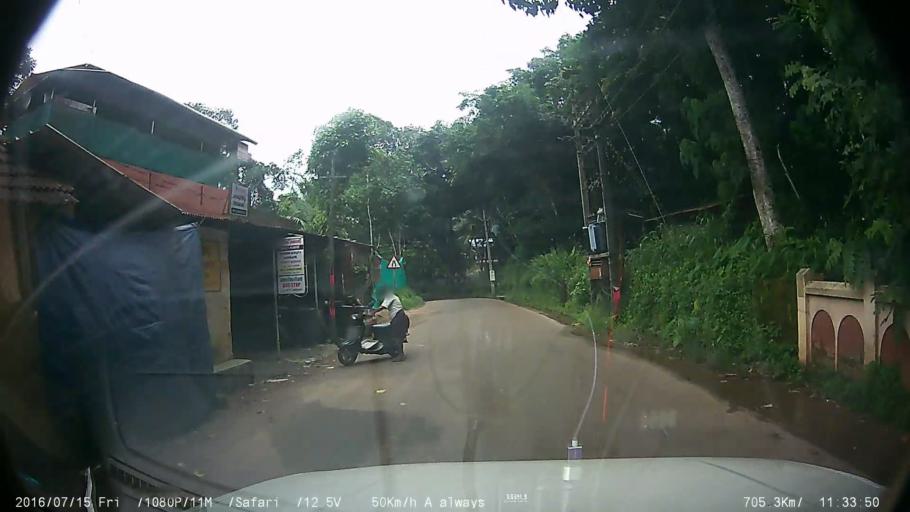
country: IN
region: Kerala
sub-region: Ernakulam
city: Piravam
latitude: 9.7863
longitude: 76.4977
